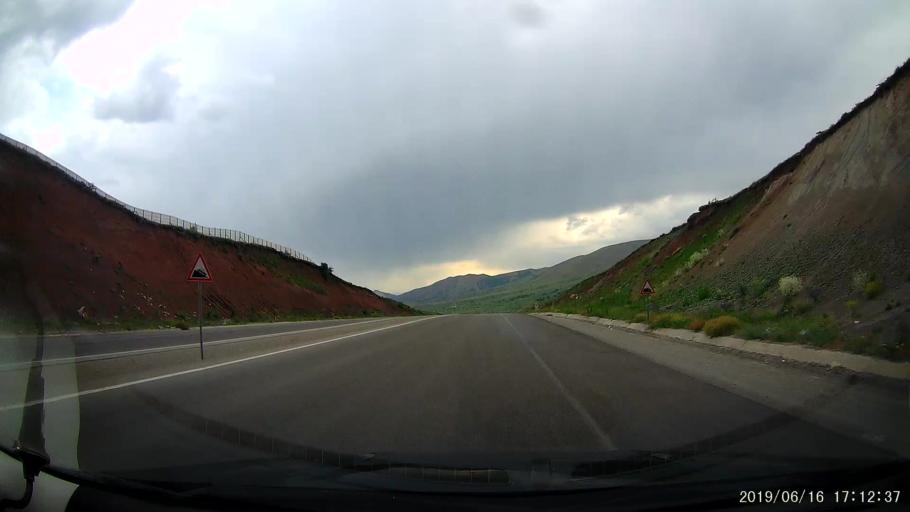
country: TR
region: Erzurum
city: Askale
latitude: 39.8593
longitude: 40.6155
